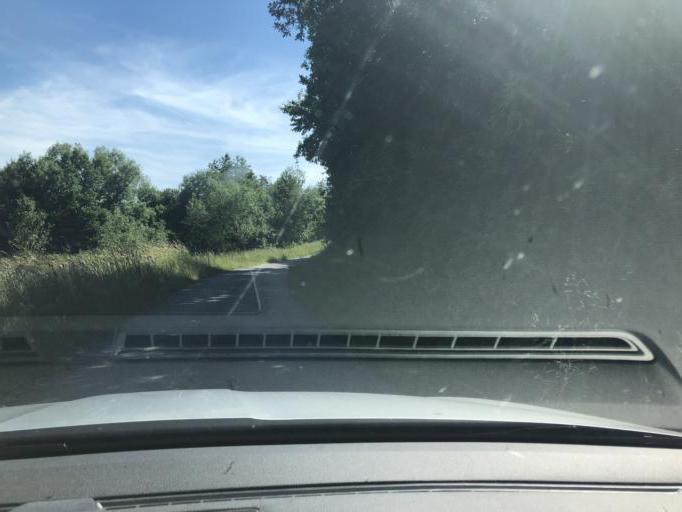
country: SE
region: Blekinge
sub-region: Karlshamns Kommun
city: Morrum
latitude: 56.1781
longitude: 14.7032
